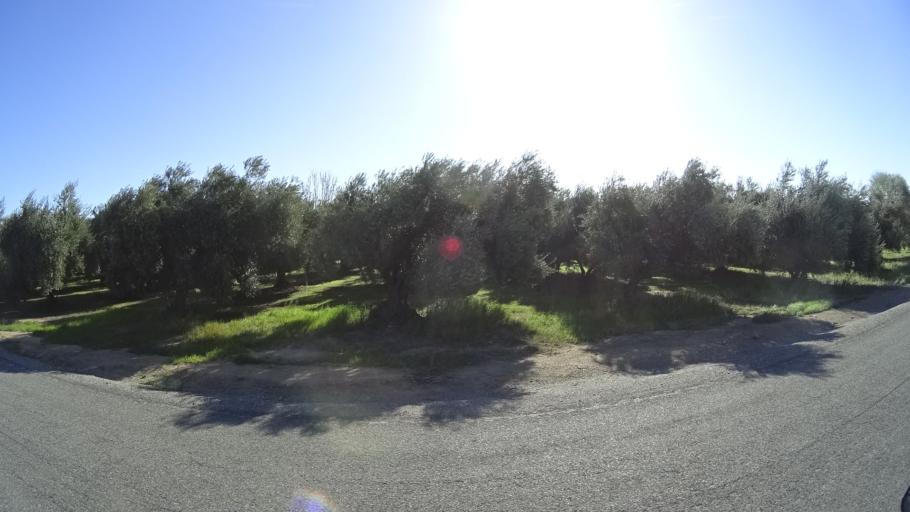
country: US
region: California
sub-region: Glenn County
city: Orland
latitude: 39.7399
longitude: -122.2390
